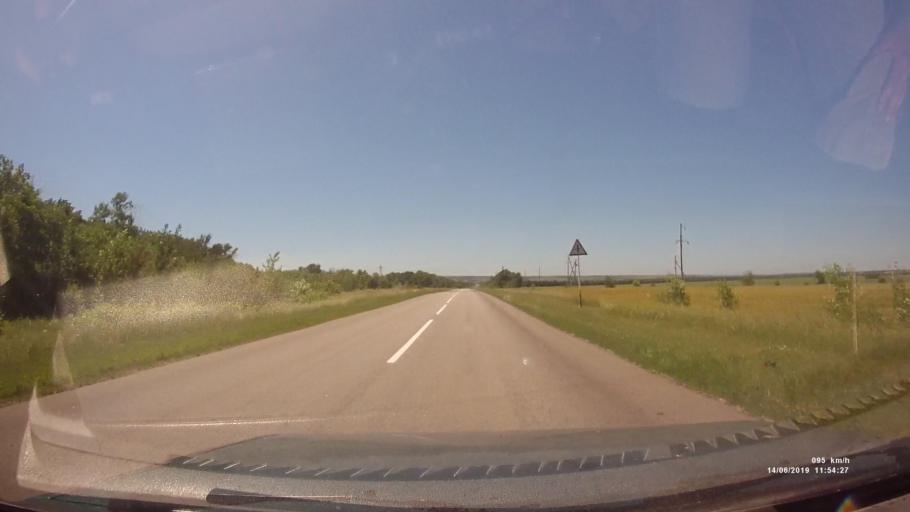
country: RU
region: Rostov
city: Kazanskaya
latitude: 49.8188
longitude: 41.1940
